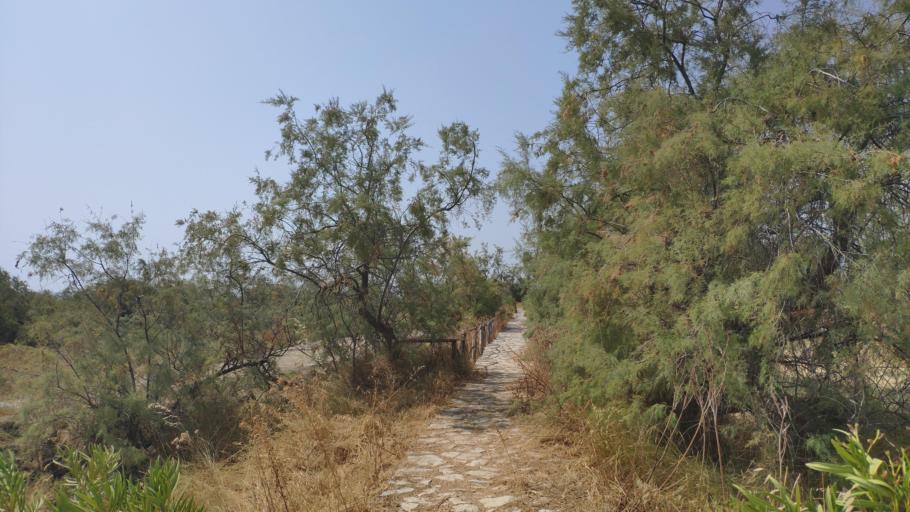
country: GR
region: West Greece
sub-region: Nomos Aitolias kai Akarnanias
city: Menidi
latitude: 39.0370
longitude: 21.0744
